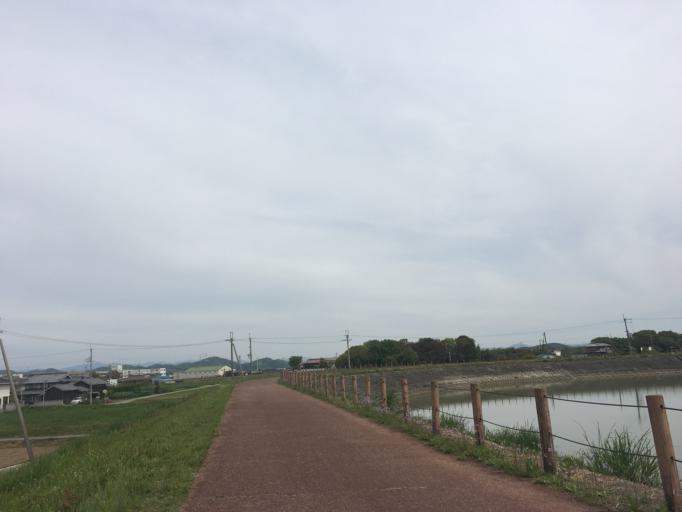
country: JP
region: Hyogo
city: Miki
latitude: 34.7700
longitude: 134.9212
